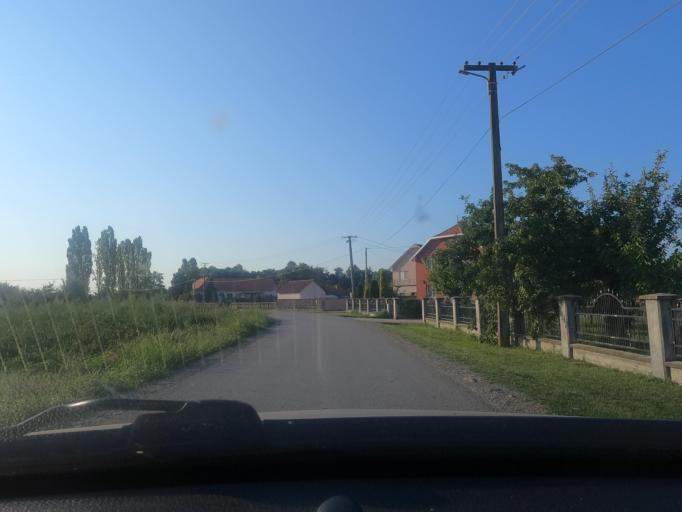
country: RS
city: Bogosavac
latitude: 44.7515
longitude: 19.5803
